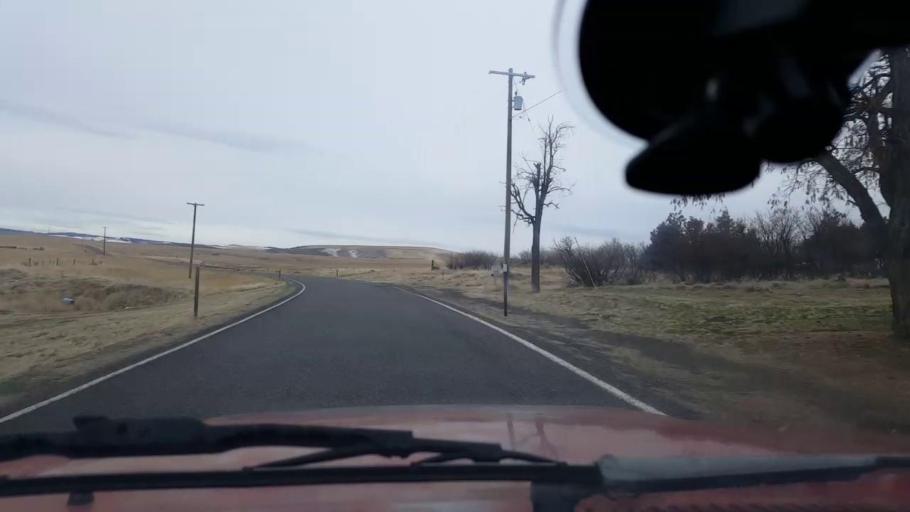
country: US
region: Washington
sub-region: Asotin County
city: Clarkston Heights-Vineland
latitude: 46.3328
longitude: -117.3164
